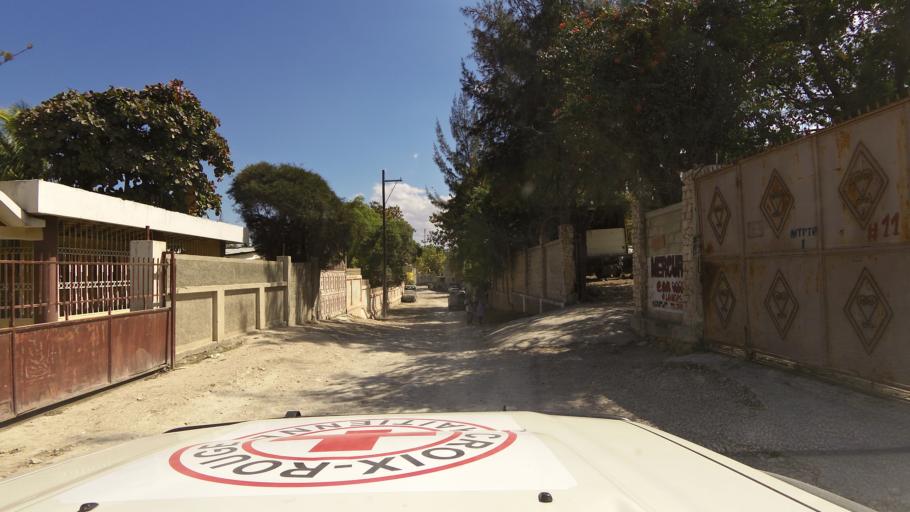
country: HT
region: Ouest
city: Delmas 73
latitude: 18.5601
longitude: -72.2960
